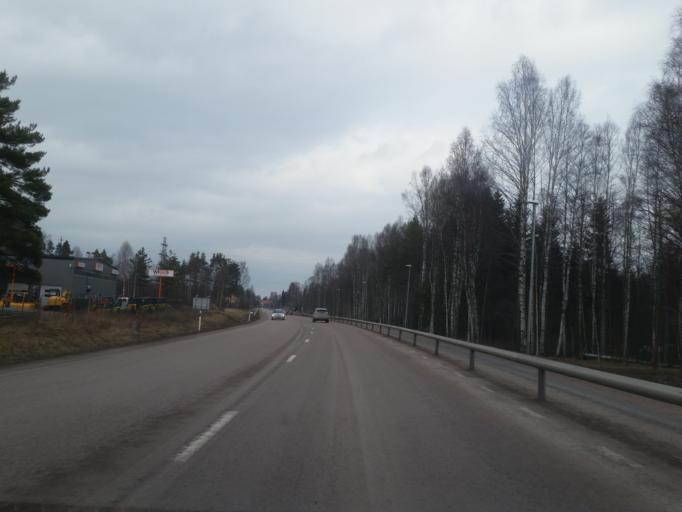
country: SE
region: Dalarna
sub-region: Mora Kommun
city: Mora
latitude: 61.0207
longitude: 14.5377
